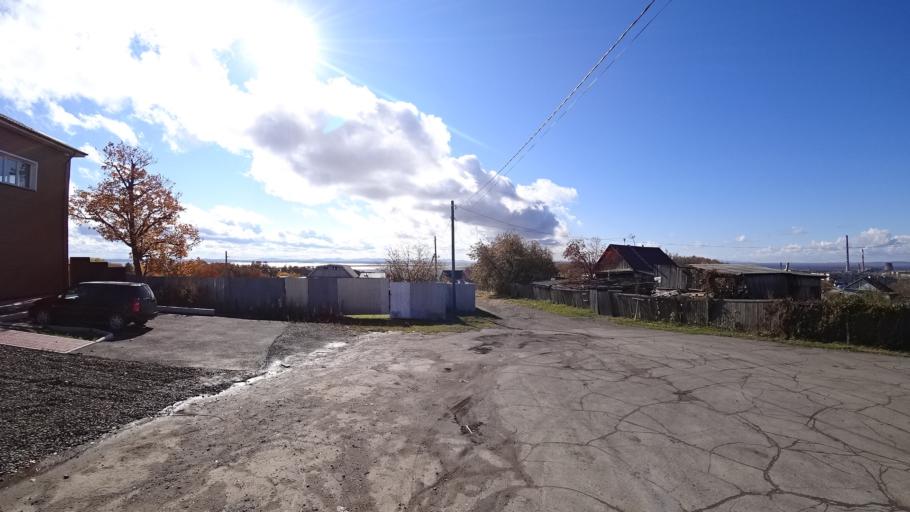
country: RU
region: Khabarovsk Krai
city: Amursk
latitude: 50.2353
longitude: 136.9228
